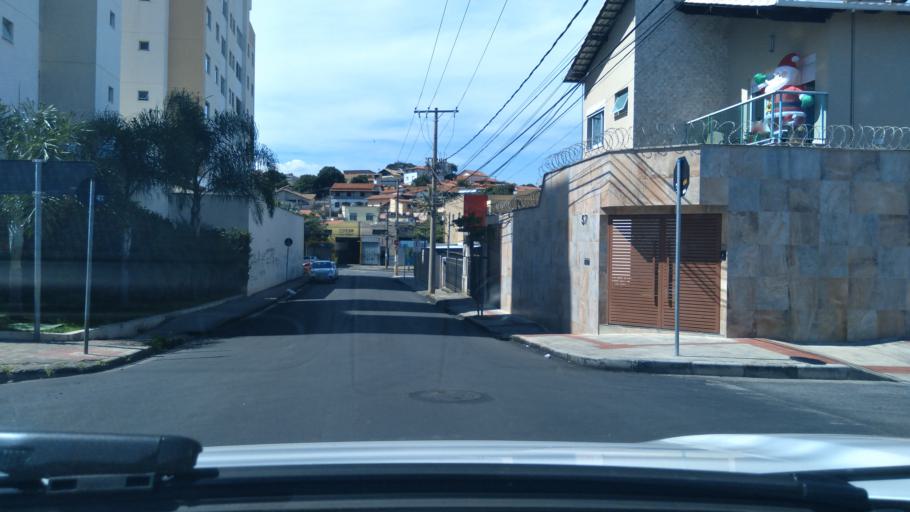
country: BR
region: Minas Gerais
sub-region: Contagem
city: Contagem
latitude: -19.9118
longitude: -44.0008
